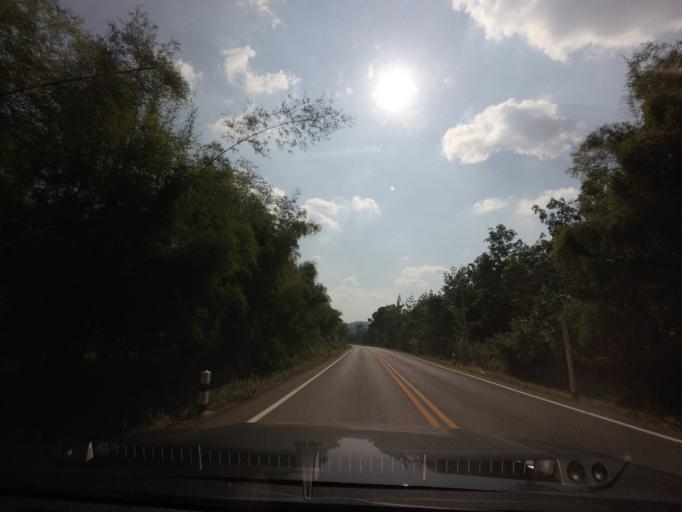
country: TH
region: Nan
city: Santi Suk
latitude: 18.9699
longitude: 100.9264
